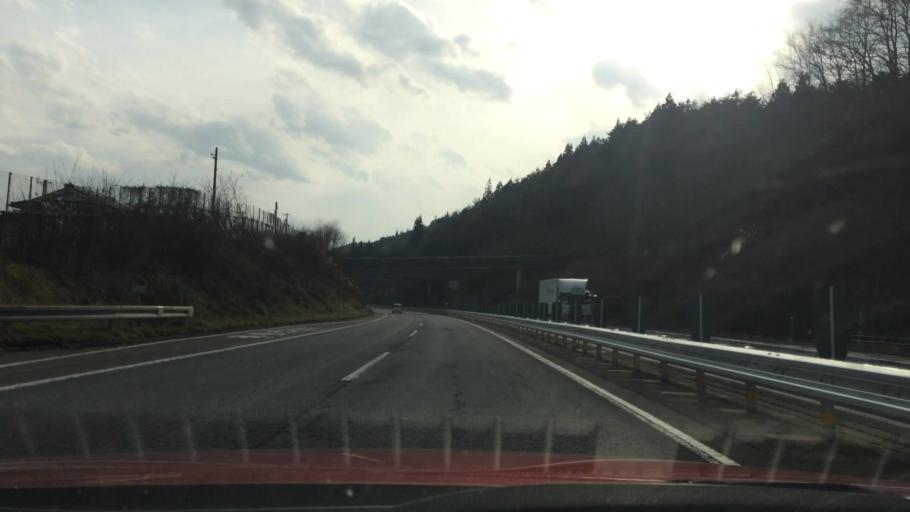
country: JP
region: Nagano
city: Iida
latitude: 35.6525
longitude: 137.8981
